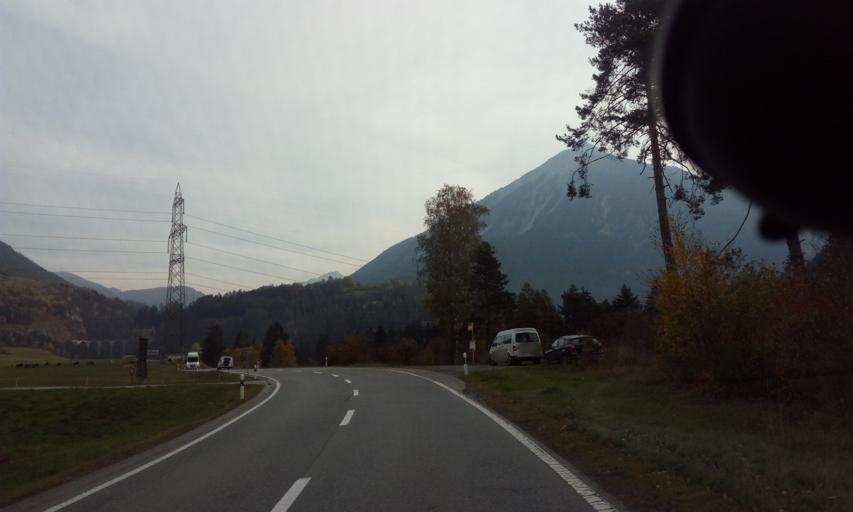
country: CH
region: Grisons
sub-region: Albula District
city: Tiefencastel
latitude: 46.6721
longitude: 9.6613
